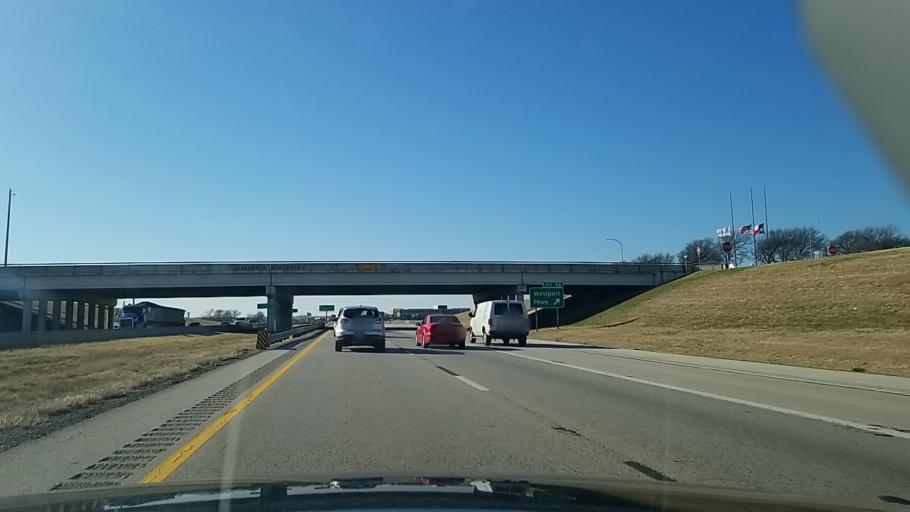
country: US
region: Texas
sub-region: Tarrant County
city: Haslet
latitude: 32.9867
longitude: -97.3028
